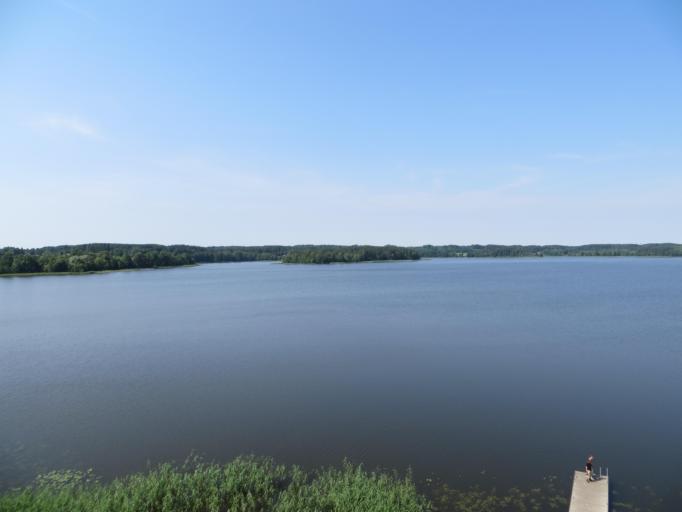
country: LT
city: Zarasai
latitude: 55.7279
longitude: 26.2438
